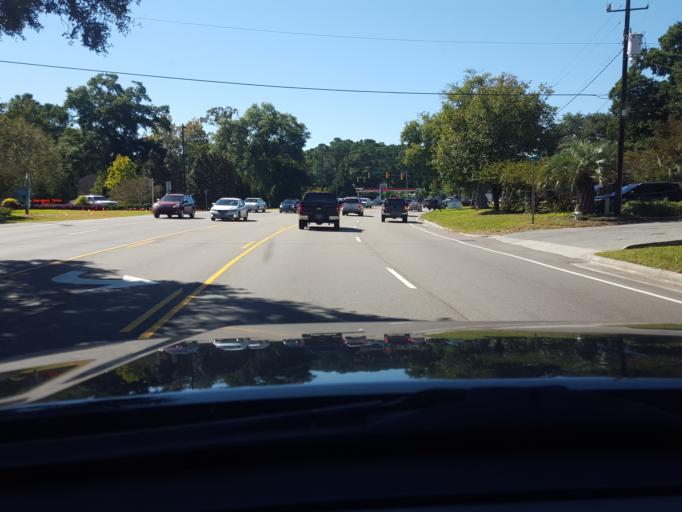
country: US
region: North Carolina
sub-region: New Hanover County
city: Seagate
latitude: 34.2113
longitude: -77.8360
